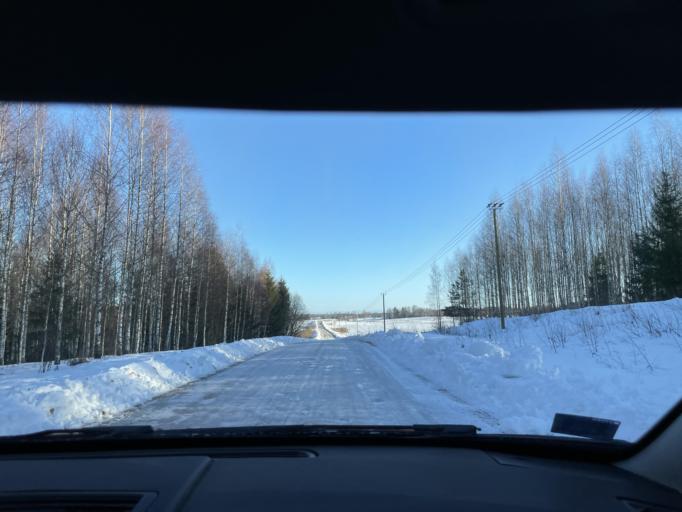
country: LV
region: Ludzas Rajons
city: Ludza
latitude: 56.4608
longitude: 27.6207
